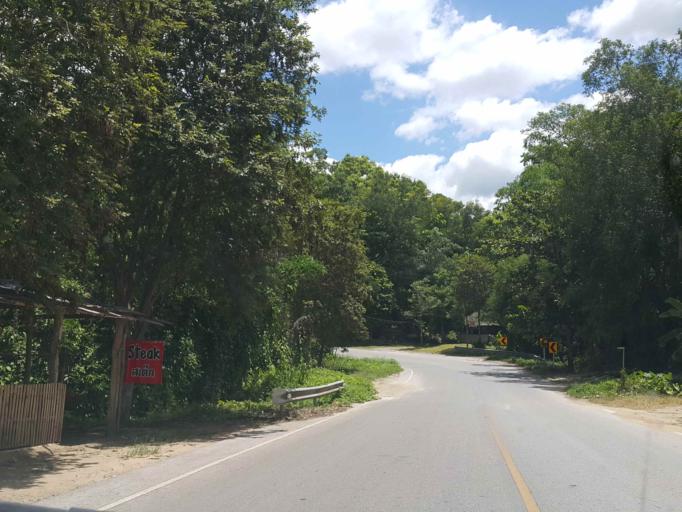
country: TH
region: Chiang Mai
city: Hang Dong
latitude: 18.7708
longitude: 98.8667
